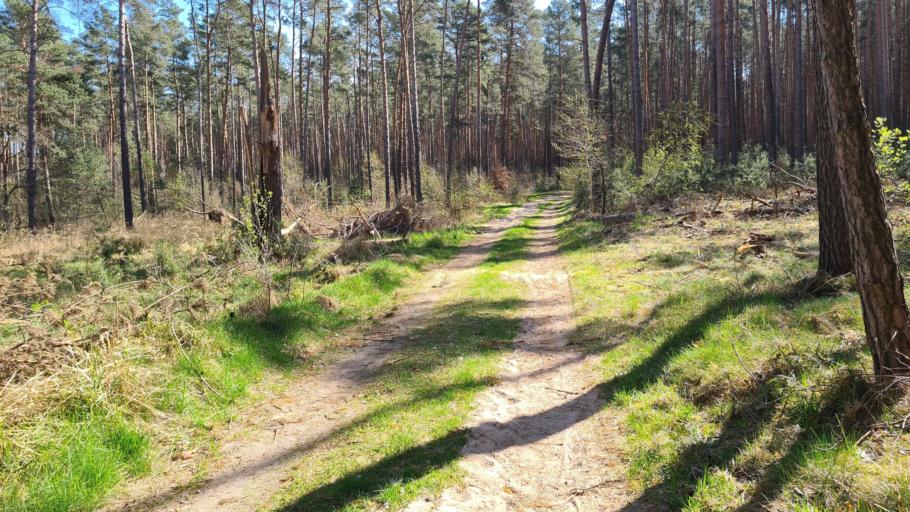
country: DE
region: Brandenburg
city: Groden
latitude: 51.3901
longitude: 13.5682
